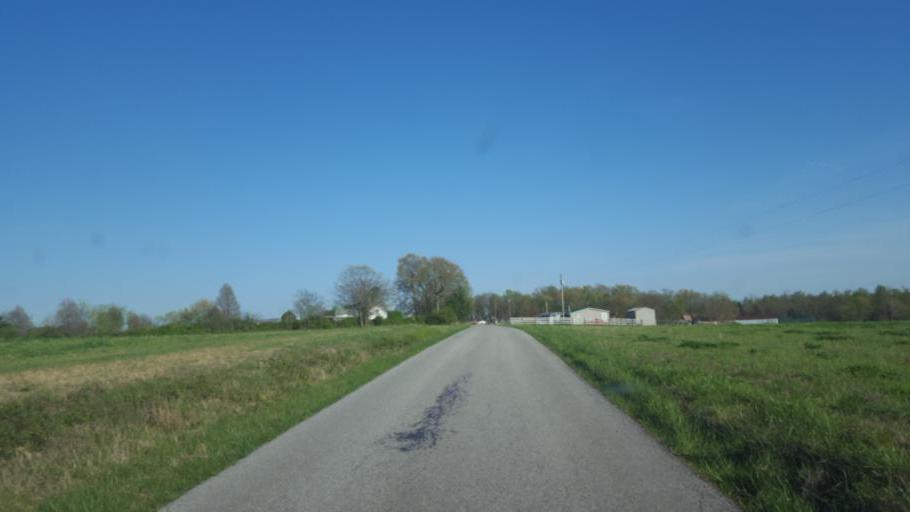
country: US
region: Kentucky
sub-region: Barren County
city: Cave City
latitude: 37.1744
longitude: -85.9961
